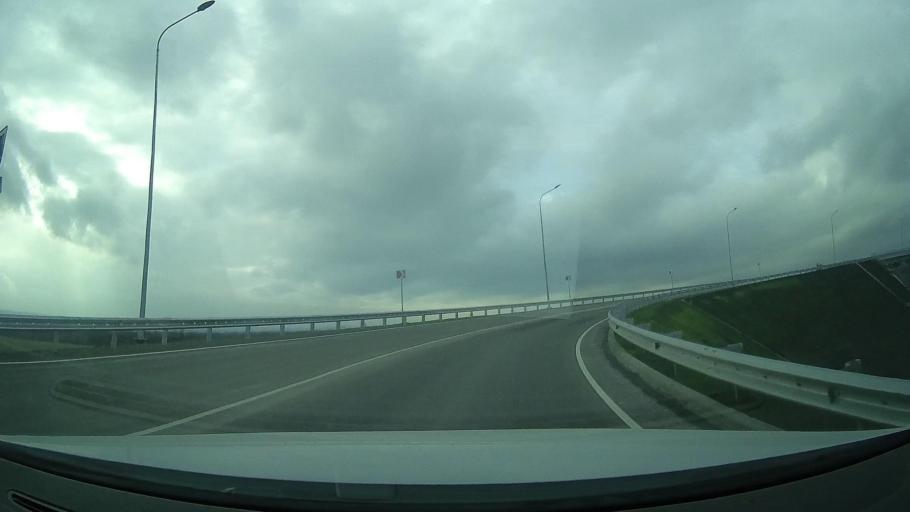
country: RU
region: Rostov
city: Grushevskaya
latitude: 47.4932
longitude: 39.9527
